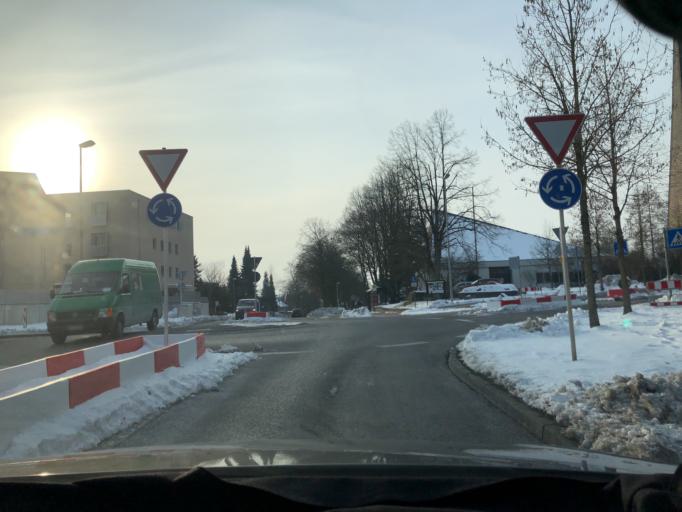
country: DE
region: Baden-Wuerttemberg
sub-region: Tuebingen Region
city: Biberach an der Riss
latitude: 48.1000
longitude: 9.7767
